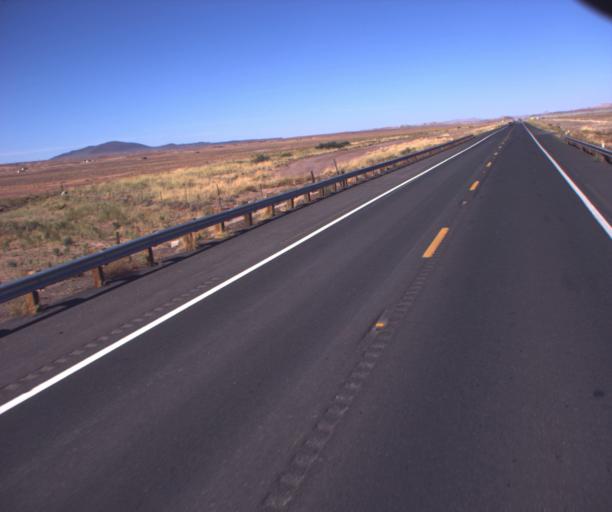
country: US
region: Arizona
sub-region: Coconino County
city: Tuba City
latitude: 35.9019
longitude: -111.4052
